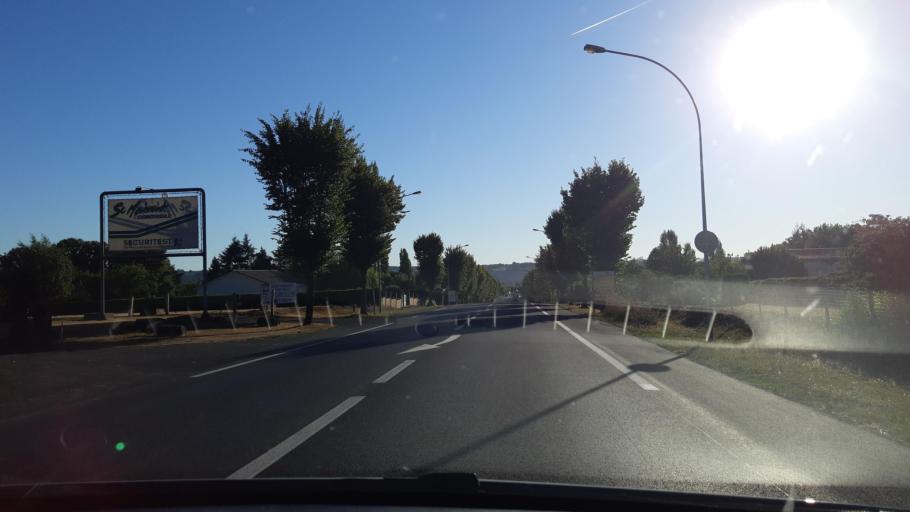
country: FR
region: Poitou-Charentes
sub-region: Departement des Deux-Sevres
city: Saivres
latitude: 46.4081
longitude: -0.2208
